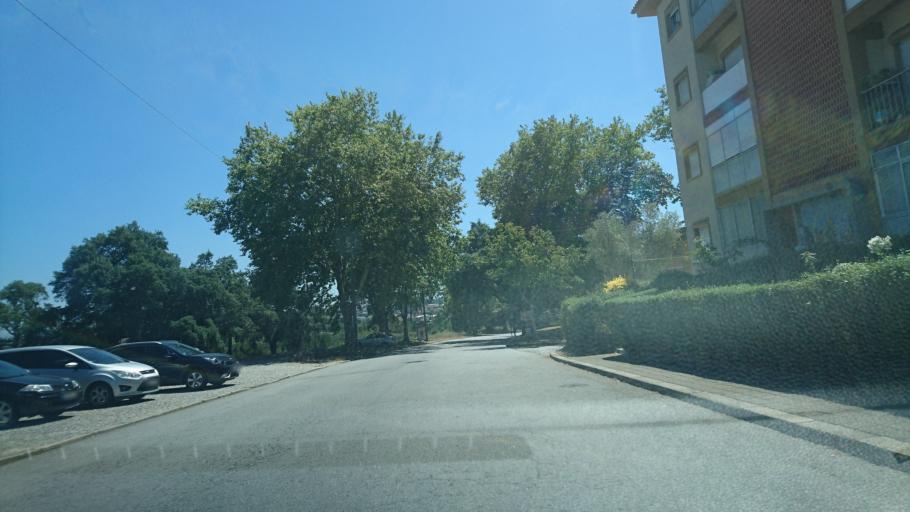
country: PT
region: Porto
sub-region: Gondomar
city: Rio Tinto
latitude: 41.1625
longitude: -8.5668
